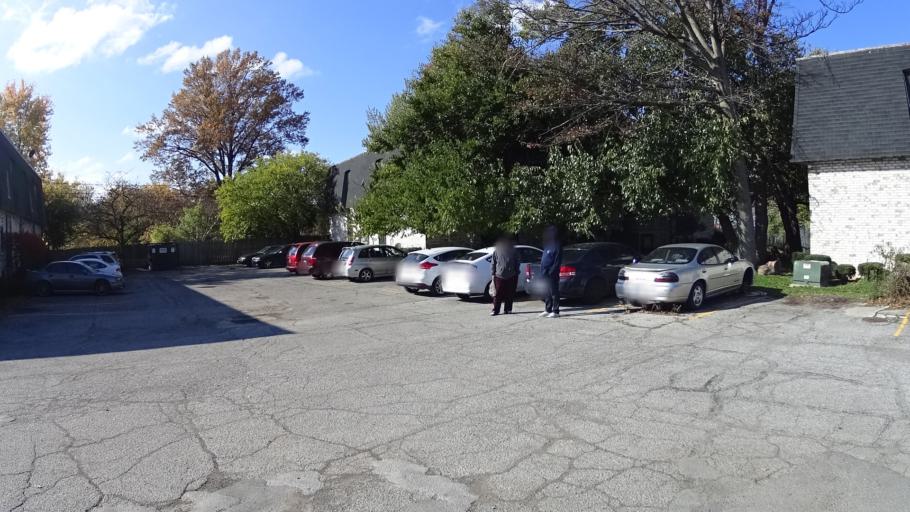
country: US
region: Ohio
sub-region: Lorain County
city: Lorain
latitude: 41.4581
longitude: -82.2054
